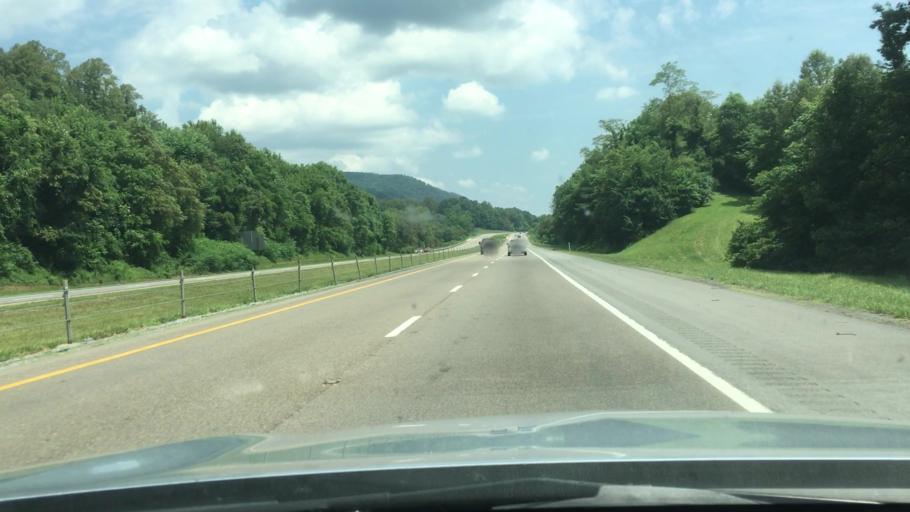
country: US
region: Tennessee
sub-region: Unicoi County
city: Unicoi
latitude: 36.2224
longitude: -82.3422
